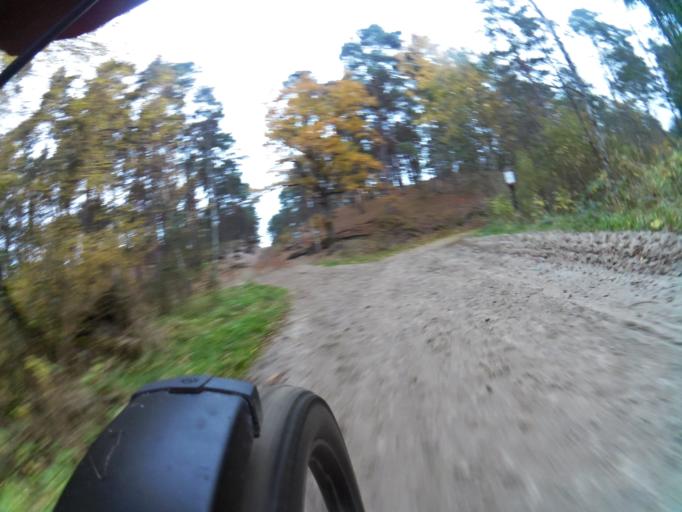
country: PL
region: Pomeranian Voivodeship
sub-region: Powiat wejherowski
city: Choczewo
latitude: 54.7828
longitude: 17.7410
